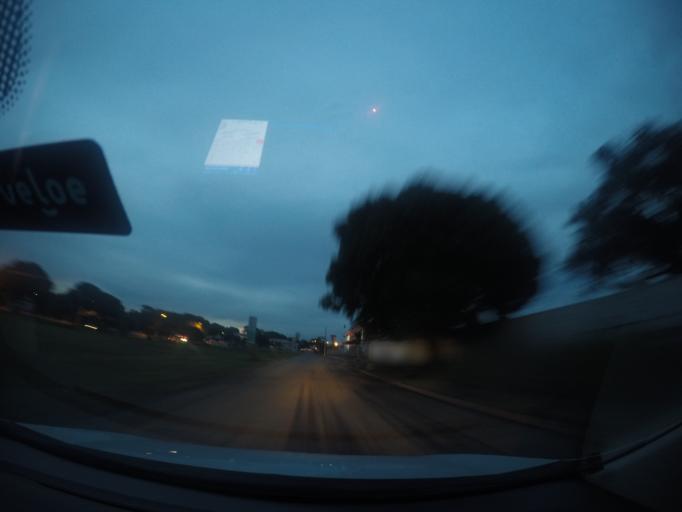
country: BR
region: Goias
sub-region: Goiania
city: Goiania
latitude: -16.6460
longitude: -49.2394
